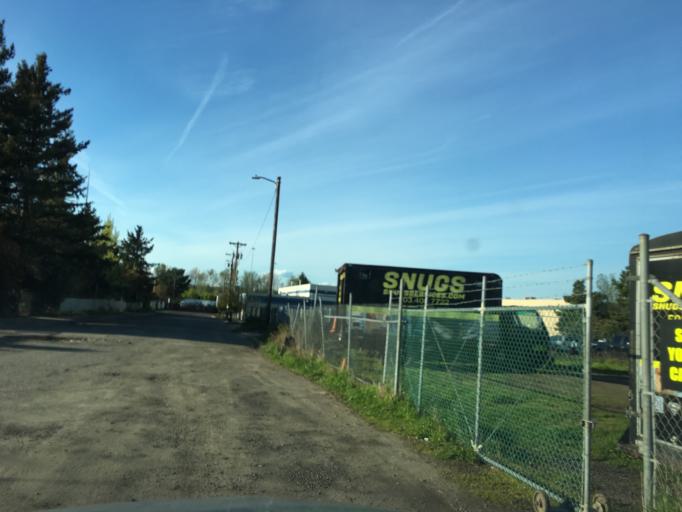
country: US
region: Oregon
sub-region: Multnomah County
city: Lents
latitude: 45.5558
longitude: -122.5224
